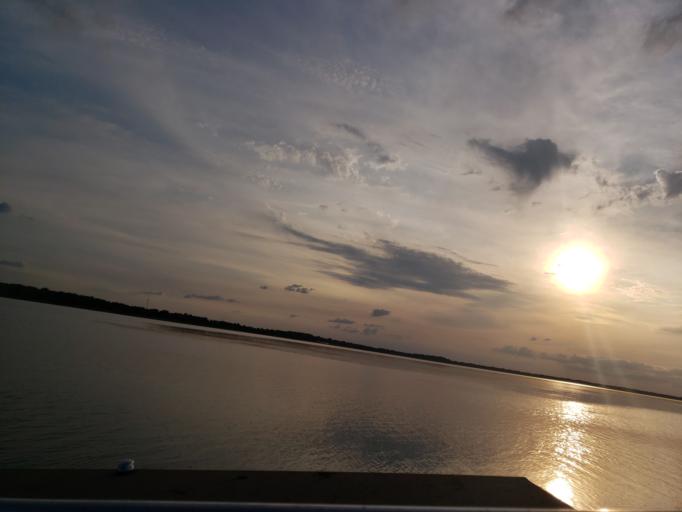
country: US
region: Florida
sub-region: Osceola County
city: Poinciana
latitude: 28.1458
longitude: -81.3558
